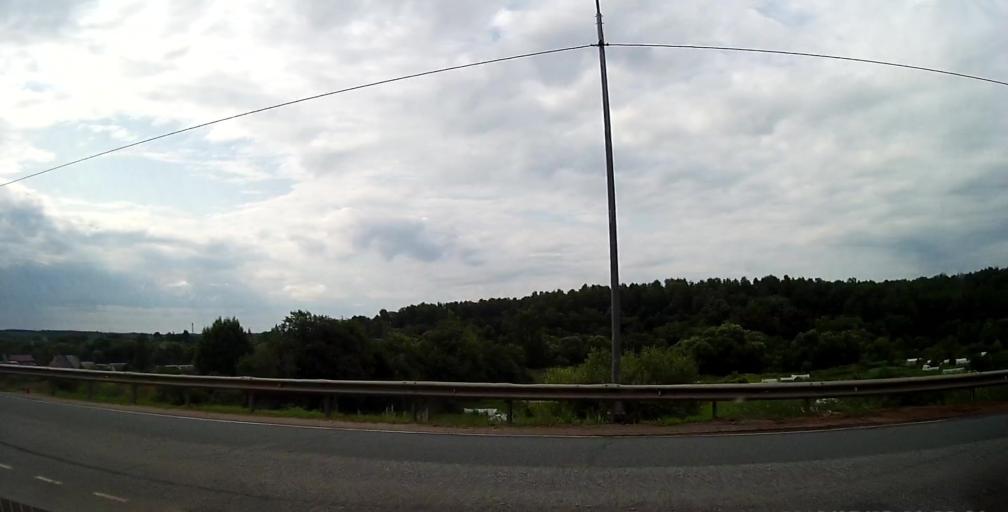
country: RU
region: Smolensk
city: Katyn'
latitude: 54.7707
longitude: 31.6838
